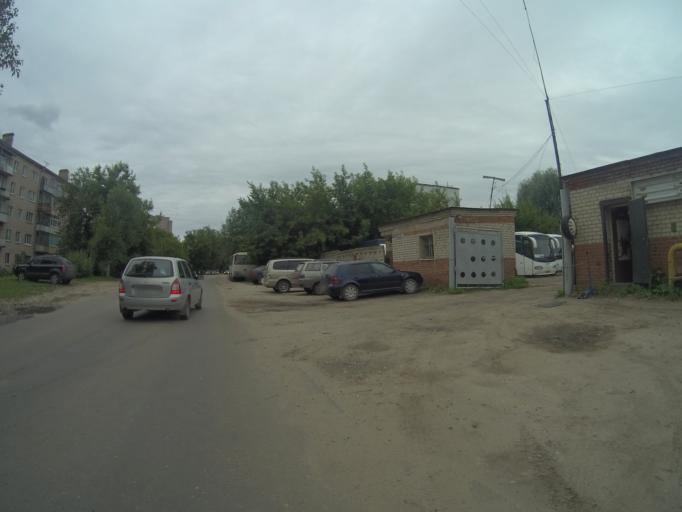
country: RU
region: Vladimir
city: Vladimir
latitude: 56.1246
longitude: 40.3713
